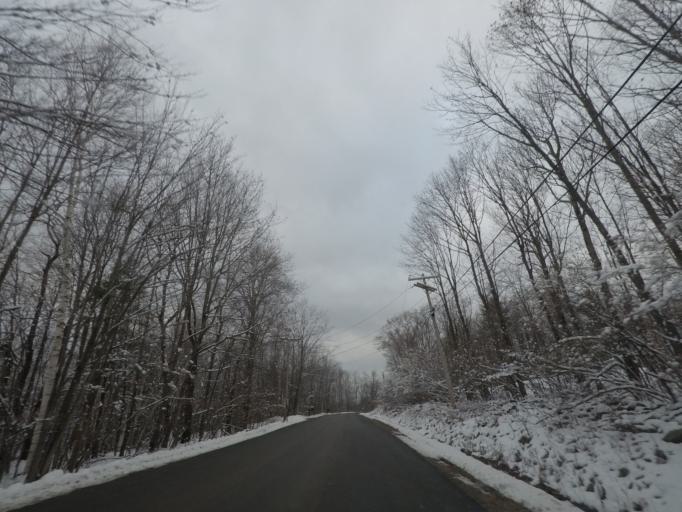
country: US
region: New York
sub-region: Rensselaer County
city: Averill Park
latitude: 42.6612
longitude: -73.5325
